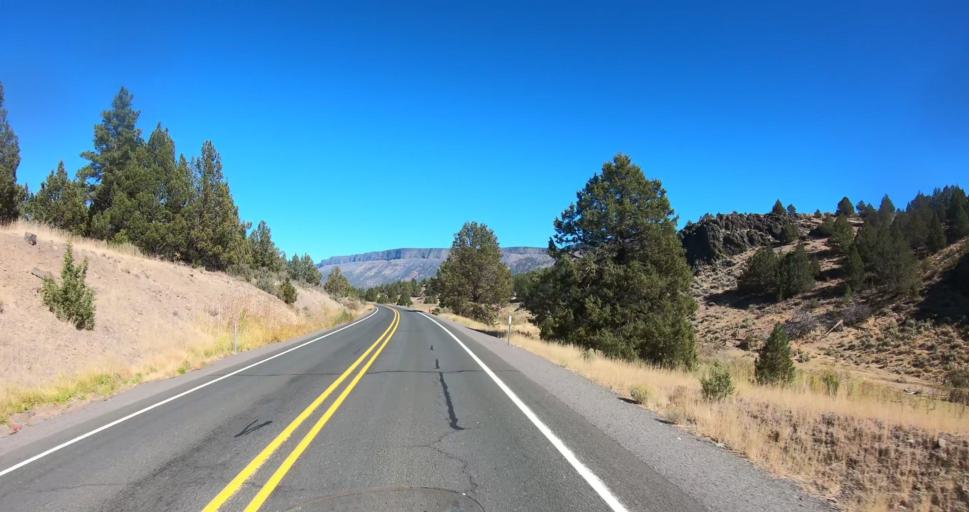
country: US
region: Oregon
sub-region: Lake County
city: Lakeview
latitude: 42.4260
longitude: -120.2855
